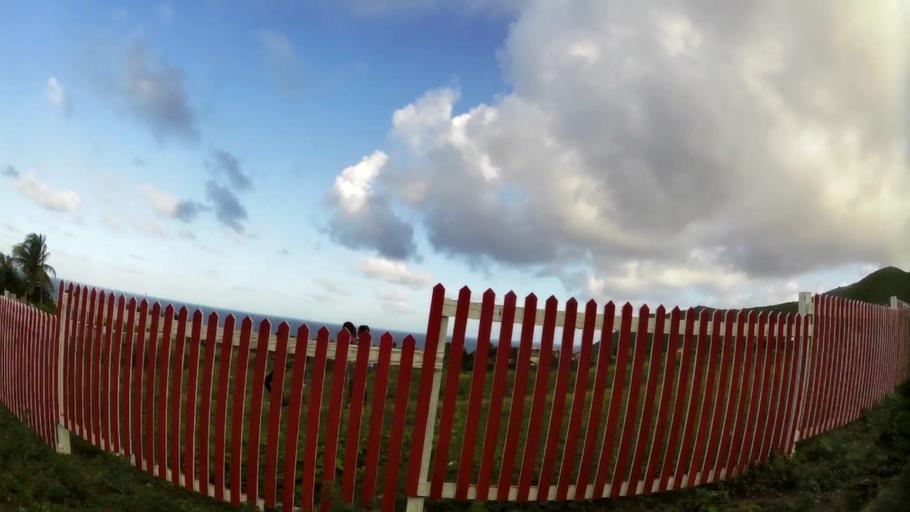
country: KN
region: Saint Mary Cayon
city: Cayon
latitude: 17.3518
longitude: -62.7303
